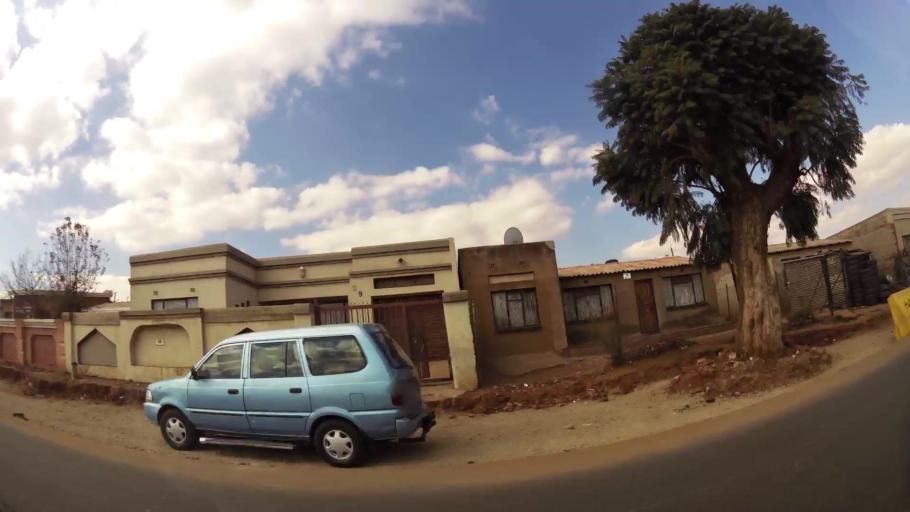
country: ZA
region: Gauteng
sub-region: Ekurhuleni Metropolitan Municipality
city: Tembisa
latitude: -26.0007
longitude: 28.2418
